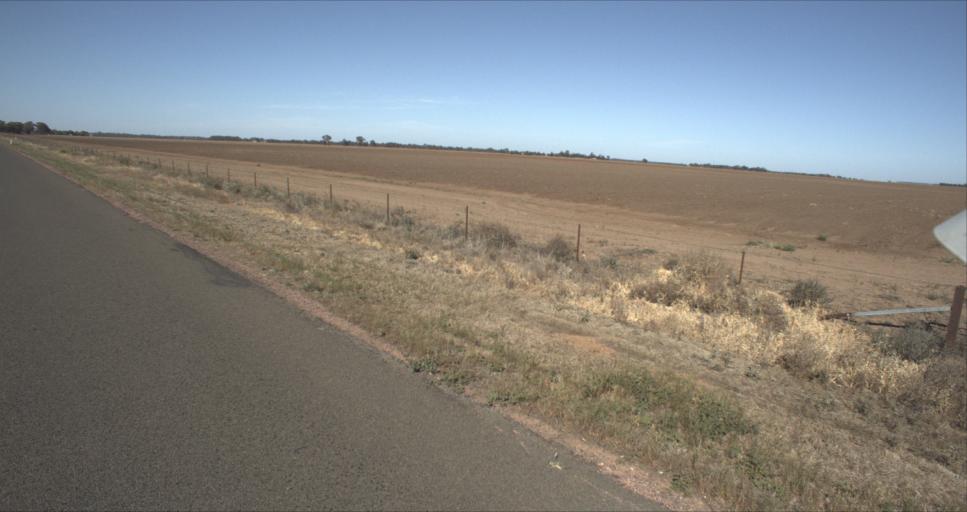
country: AU
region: New South Wales
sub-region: Leeton
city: Leeton
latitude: -34.5670
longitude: 146.2642
